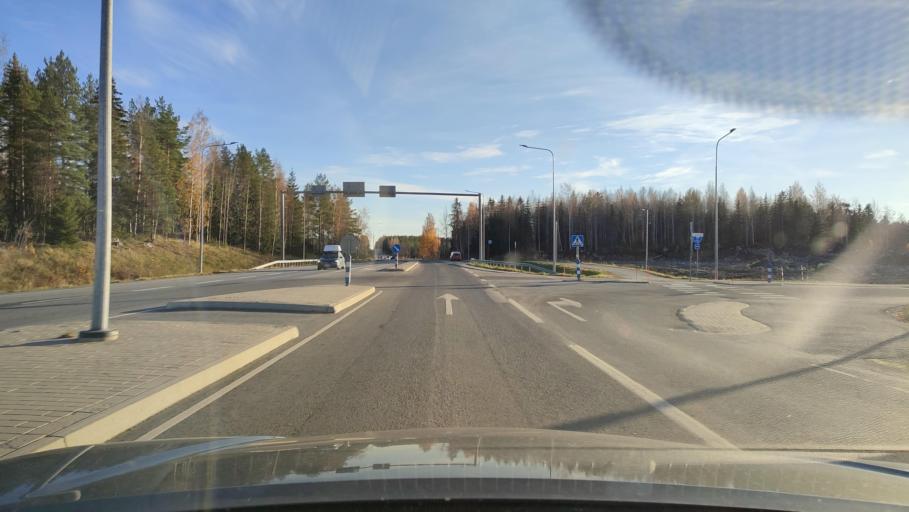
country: FI
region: Ostrobothnia
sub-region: Vaasa
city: Ristinummi
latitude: 63.0247
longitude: 21.7565
